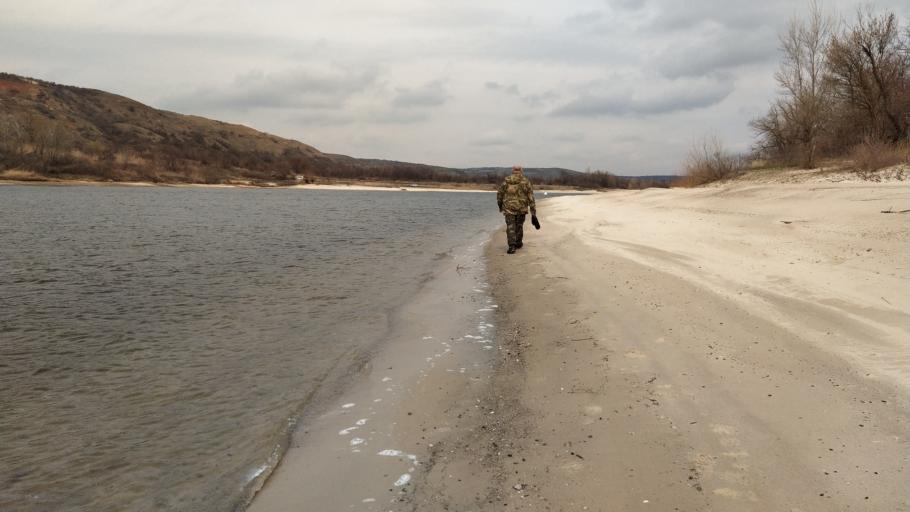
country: RU
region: Rostov
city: Semikarakorsk
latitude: 47.5596
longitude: 40.6733
